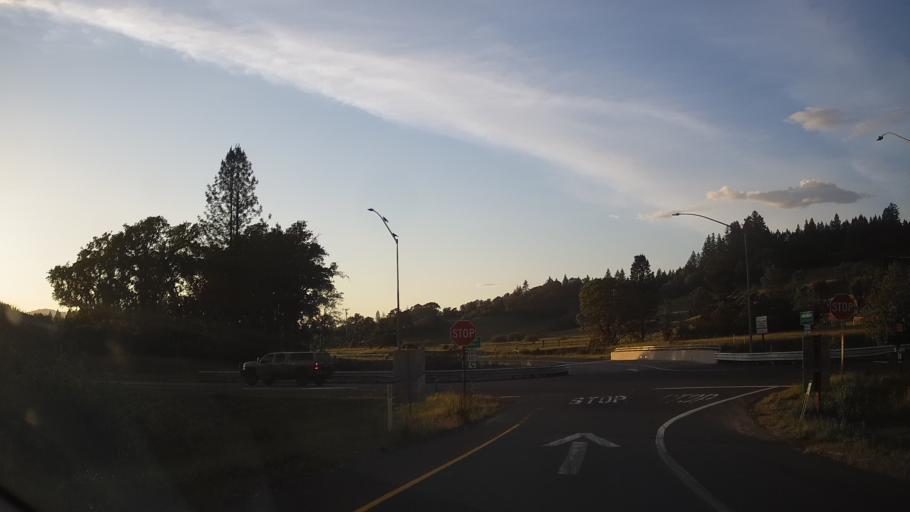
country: US
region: California
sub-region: Mendocino County
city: Willits
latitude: 39.3751
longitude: -123.3237
